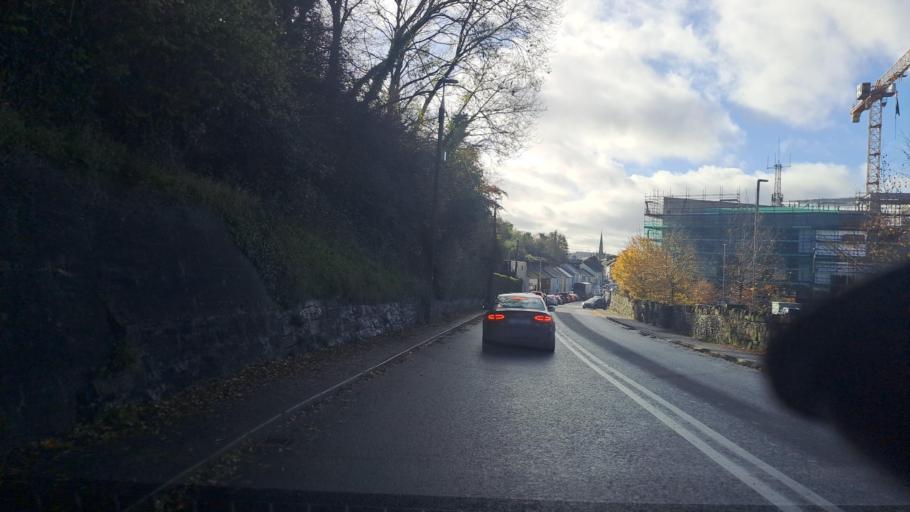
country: IE
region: Ulster
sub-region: County Monaghan
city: Monaghan
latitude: 54.2526
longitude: -6.9657
